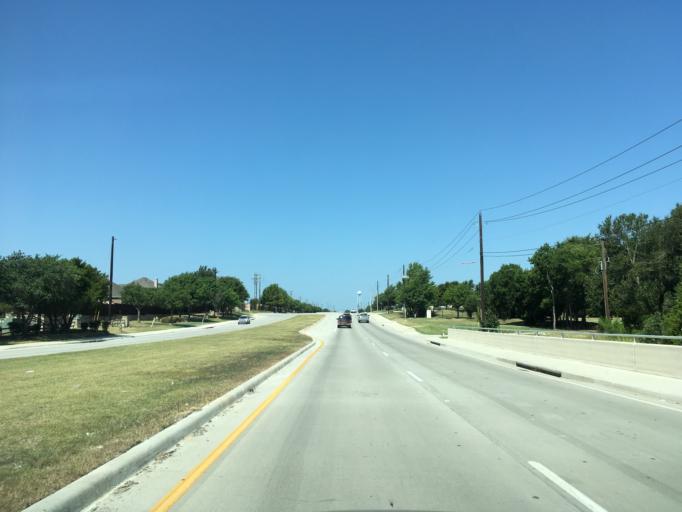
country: US
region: Texas
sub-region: Collin County
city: Fairview
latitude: 33.1297
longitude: -96.6351
